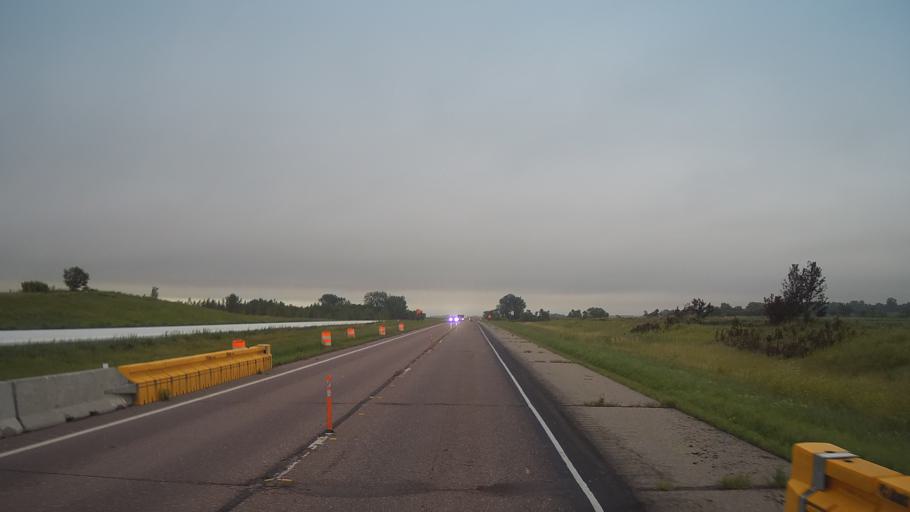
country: US
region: Minnesota
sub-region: Faribault County
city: Winnebago
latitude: 43.6661
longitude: -94.2865
